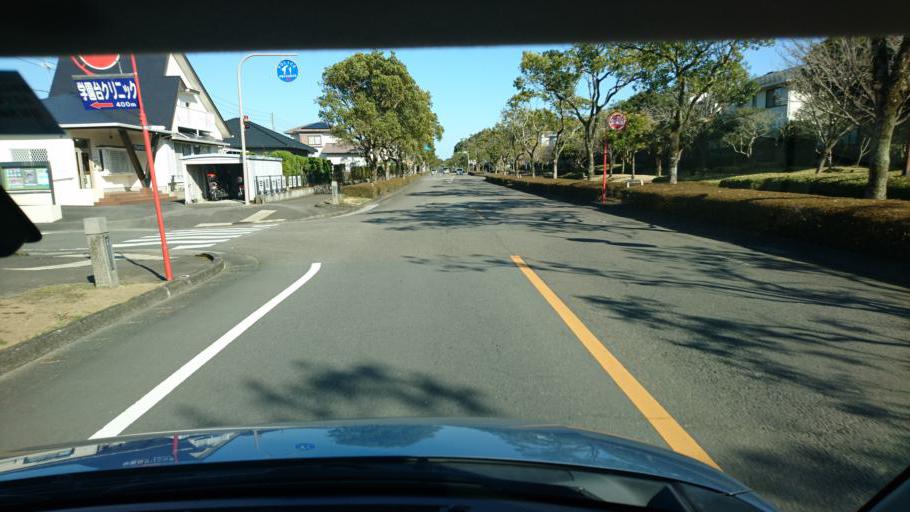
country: JP
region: Miyazaki
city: Miyazaki-shi
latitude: 31.8318
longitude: 131.4242
